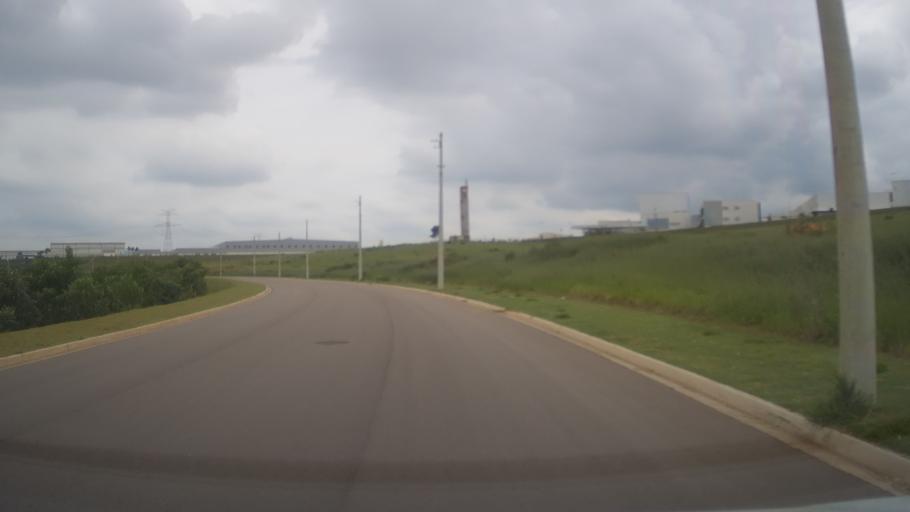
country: BR
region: Sao Paulo
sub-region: Itupeva
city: Itupeva
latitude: -23.1524
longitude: -46.9982
